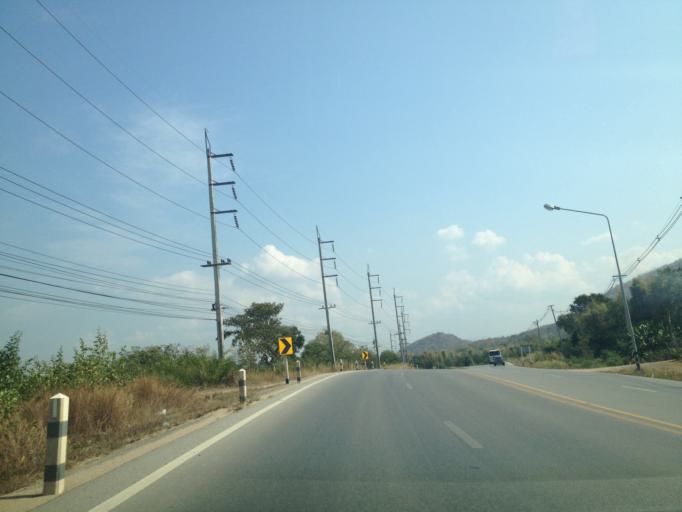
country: TH
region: Chiang Mai
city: Hot
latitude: 18.2505
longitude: 98.6072
